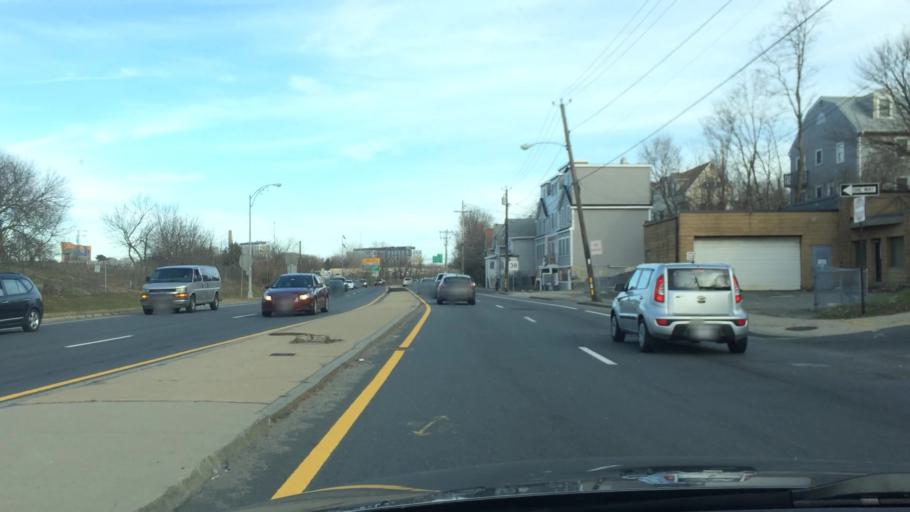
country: US
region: Massachusetts
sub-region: Middlesex County
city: Somerville
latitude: 42.3999
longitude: -71.0955
